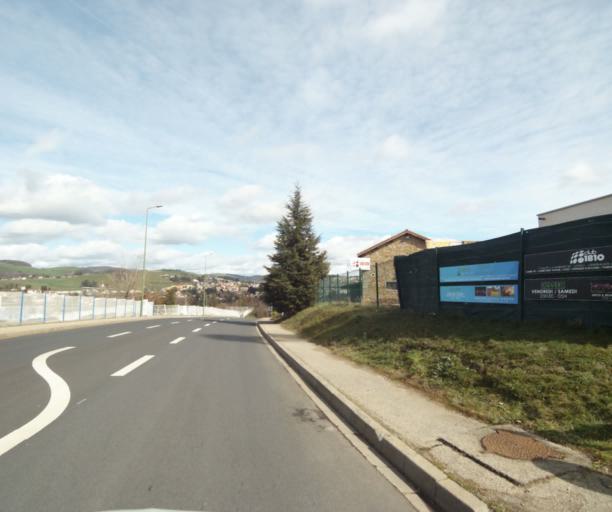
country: FR
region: Rhone-Alpes
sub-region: Departement de la Loire
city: La Talaudiere
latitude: 45.4697
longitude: 4.4225
